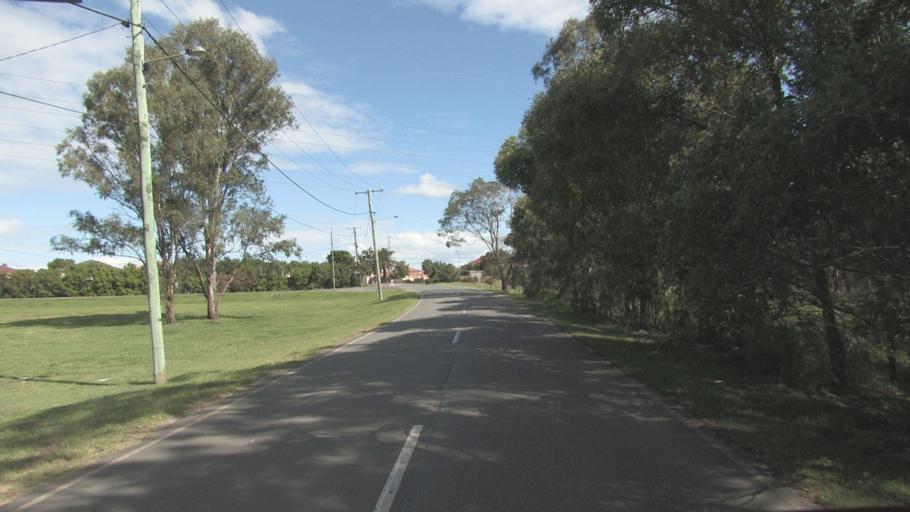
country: AU
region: Queensland
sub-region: Logan
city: Slacks Creek
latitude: -27.6573
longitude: 153.1457
